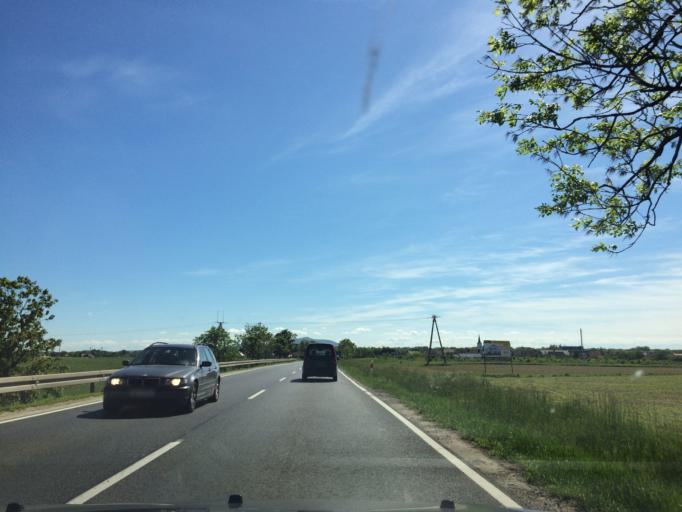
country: PL
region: Lower Silesian Voivodeship
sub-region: Powiat wroclawski
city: Gniechowice
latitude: 50.9942
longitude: 16.8441
